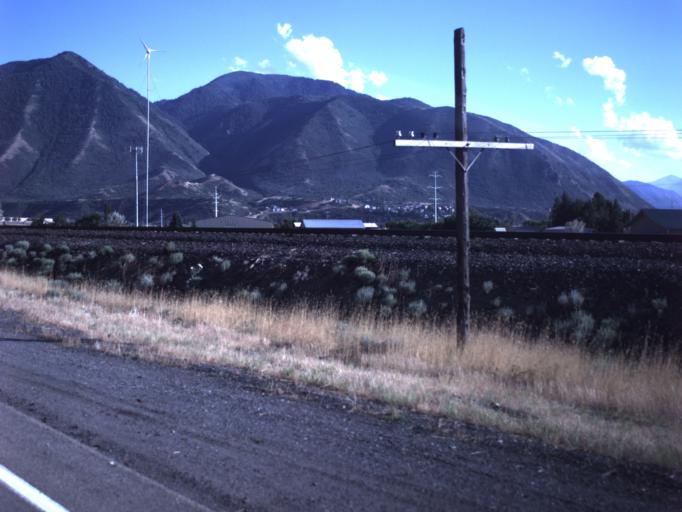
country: US
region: Utah
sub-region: Utah County
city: Mapleton
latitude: 40.1004
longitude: -111.5956
